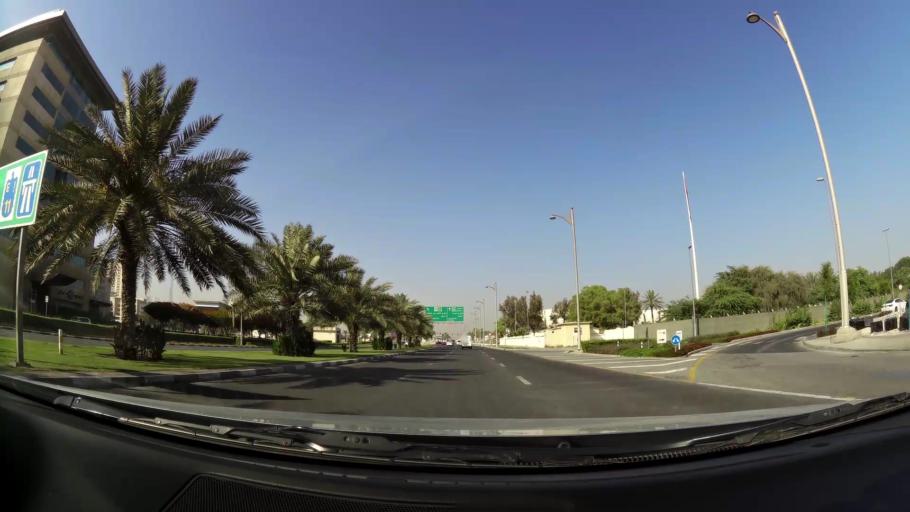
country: AE
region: Ash Shariqah
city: Sharjah
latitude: 25.2425
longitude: 55.2710
